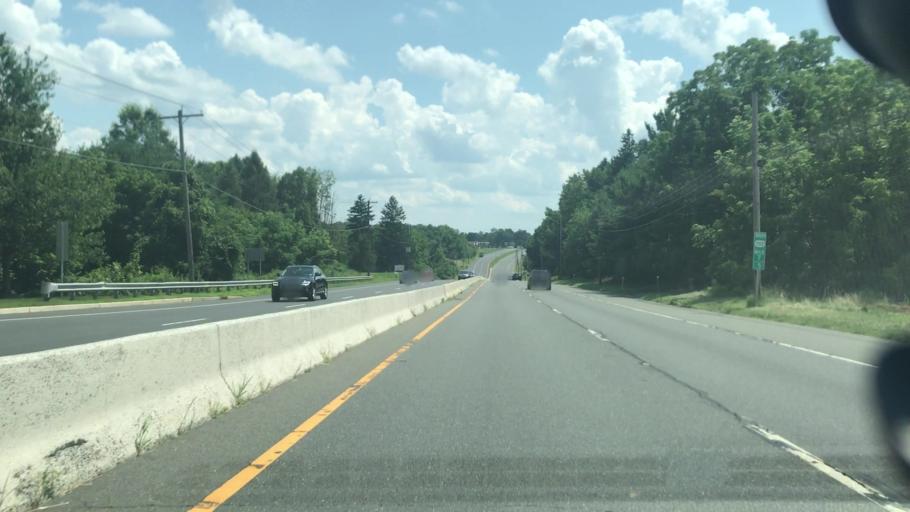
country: US
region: New Jersey
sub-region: Hunterdon County
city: Flemington
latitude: 40.4486
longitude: -74.8587
